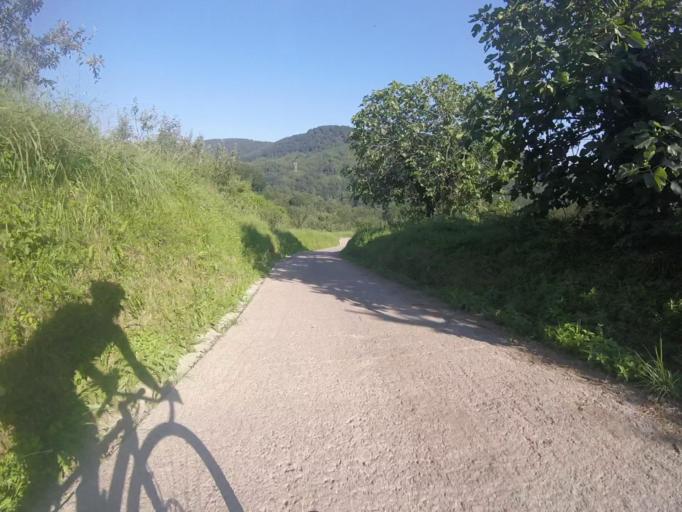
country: ES
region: Basque Country
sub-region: Provincia de Guipuzcoa
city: Astigarraga
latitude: 43.2565
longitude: -1.9403
